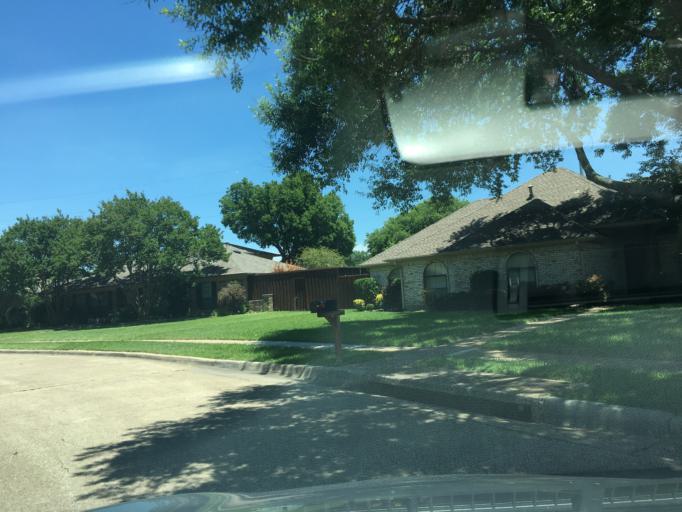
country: US
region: Texas
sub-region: Dallas County
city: Richardson
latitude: 32.9481
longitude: -96.6837
